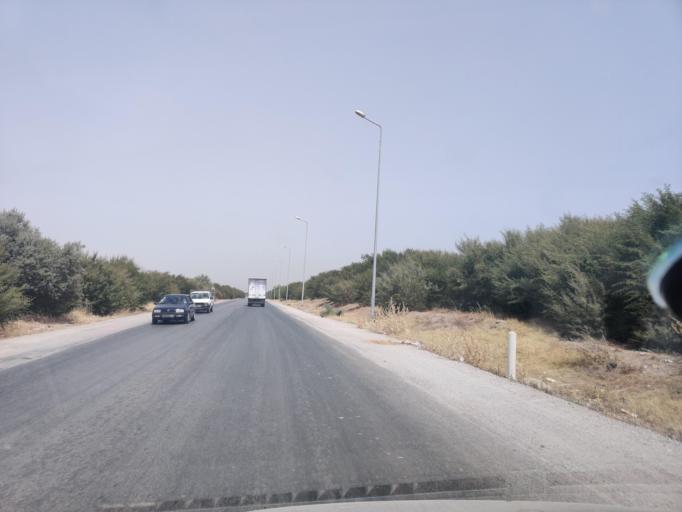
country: TN
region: Tunis
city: La Sebala du Mornag
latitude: 36.6666
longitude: 10.3251
